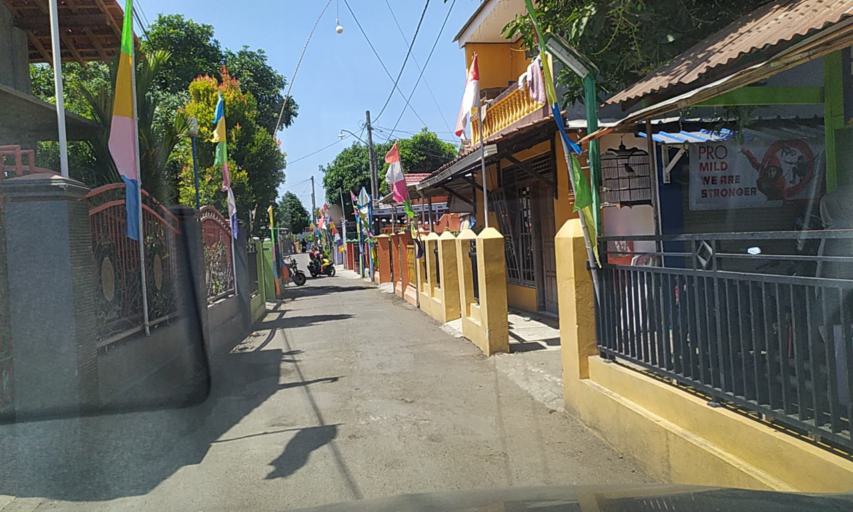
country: ID
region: Central Java
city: Karangbadar Kidul
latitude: -7.7189
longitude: 109.0089
